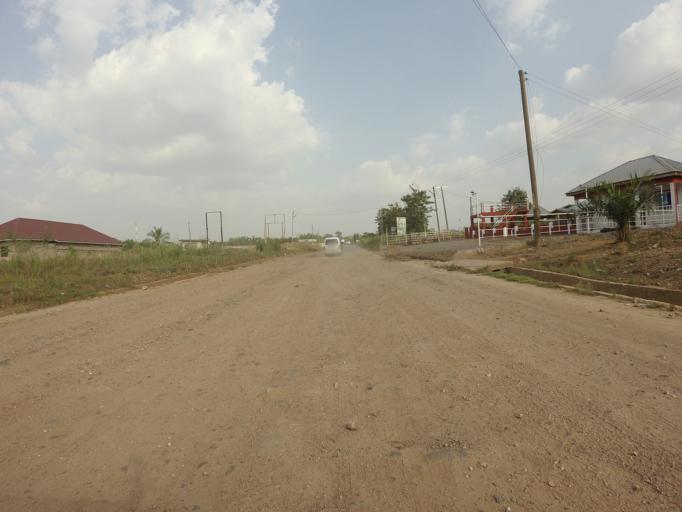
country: GH
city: Akropong
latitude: 6.2432
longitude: 0.1183
